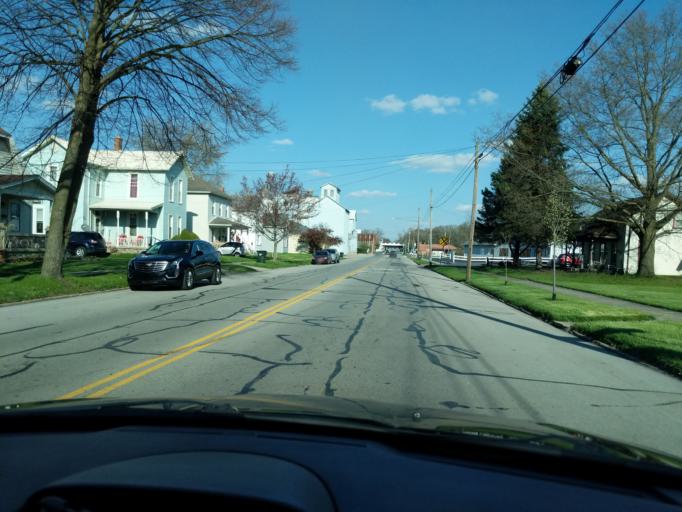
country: US
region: Ohio
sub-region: Champaign County
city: Urbana
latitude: 40.1088
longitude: -83.7634
